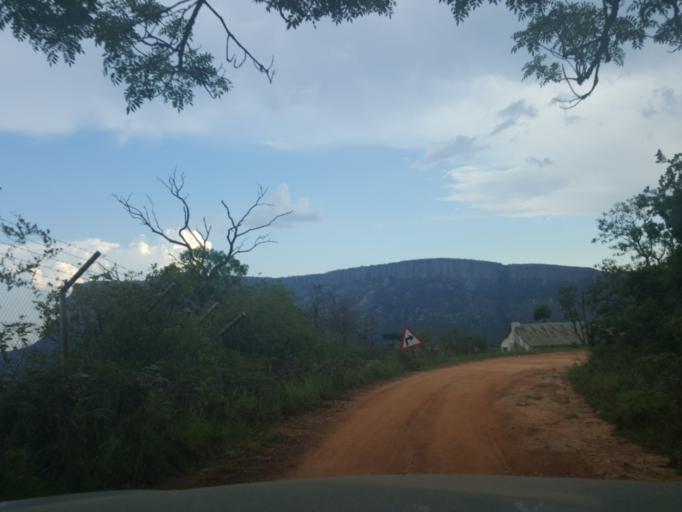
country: ZA
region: Limpopo
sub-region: Mopani District Municipality
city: Hoedspruit
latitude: -24.5807
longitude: 30.8639
